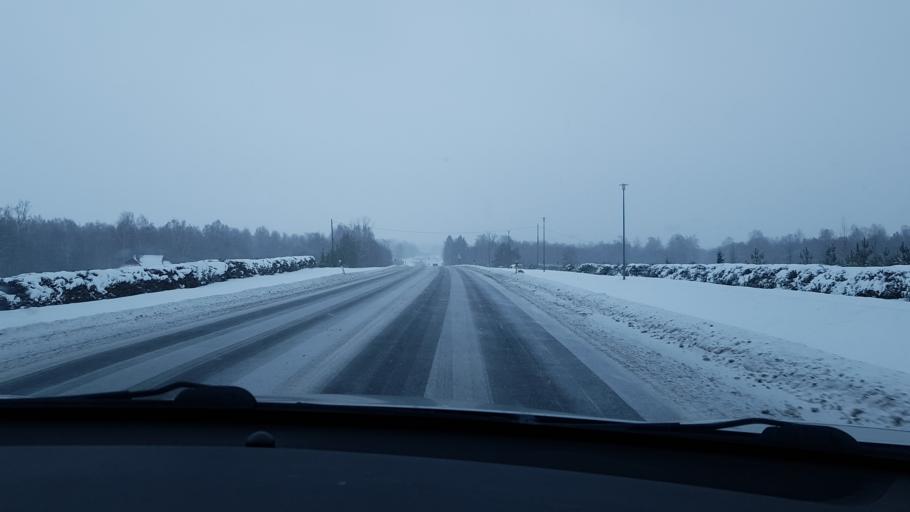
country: EE
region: Jaervamaa
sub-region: Tueri vald
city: Tueri
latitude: 58.8400
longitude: 25.4748
